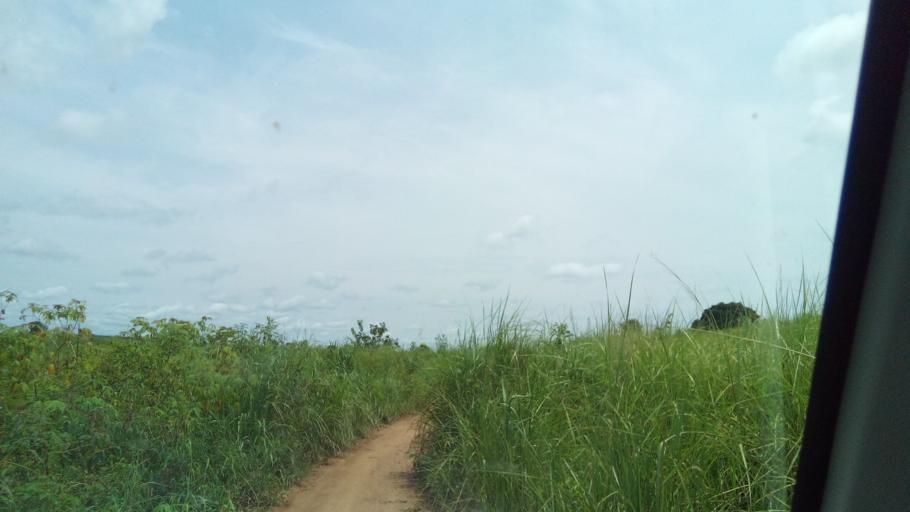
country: AO
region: Zaire
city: Mbanza Congo
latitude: -5.7975
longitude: 13.9952
